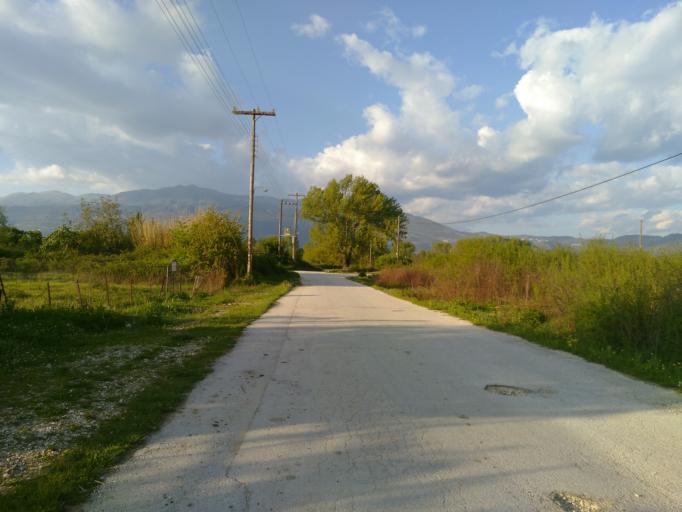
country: GR
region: Epirus
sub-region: Nomos Ioanninon
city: Katsikas
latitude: 39.6269
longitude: 20.8884
